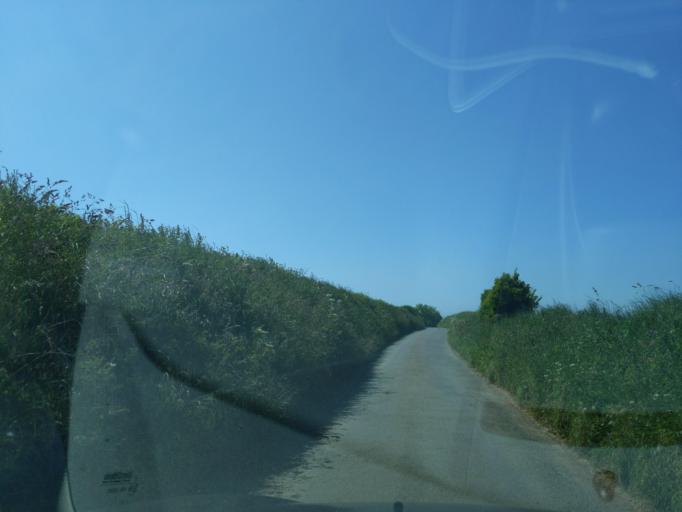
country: GB
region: England
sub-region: Cornwall
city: Wadebridge
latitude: 50.5819
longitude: -4.8390
